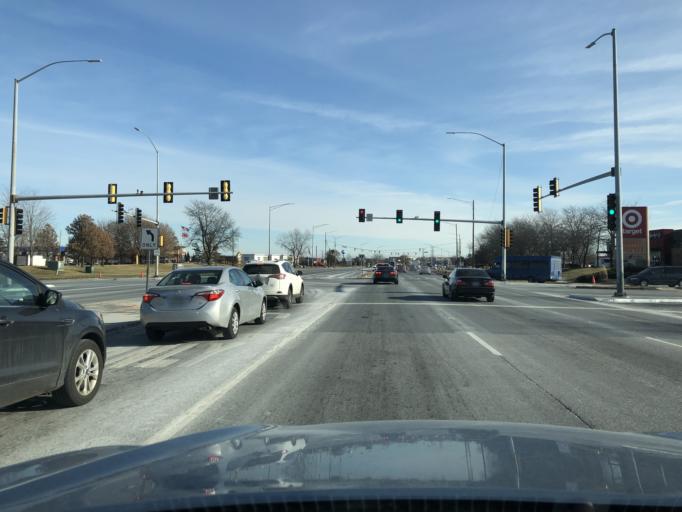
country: US
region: Illinois
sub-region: Lake County
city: Grandwood Park
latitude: 42.3855
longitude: -87.9666
